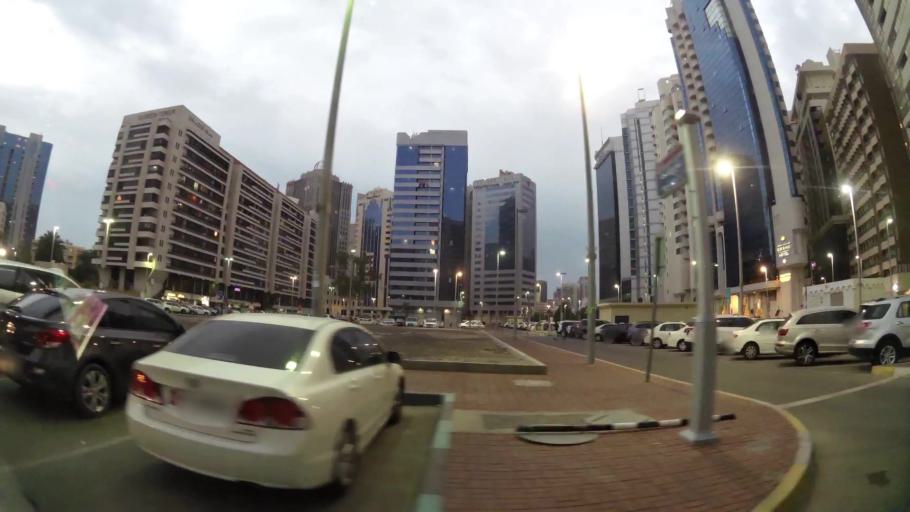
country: AE
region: Abu Dhabi
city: Abu Dhabi
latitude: 24.4923
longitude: 54.3654
